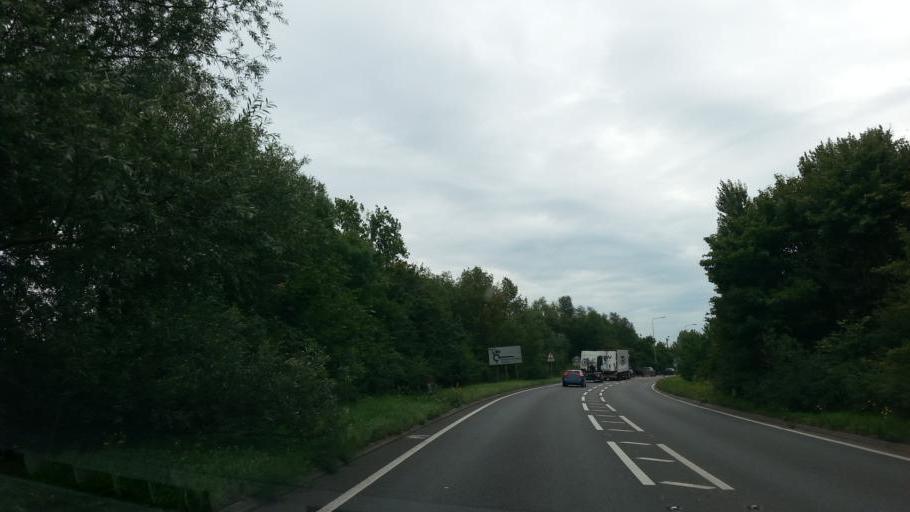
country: GB
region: England
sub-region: Cambridgeshire
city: March
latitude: 52.6086
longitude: 0.0653
